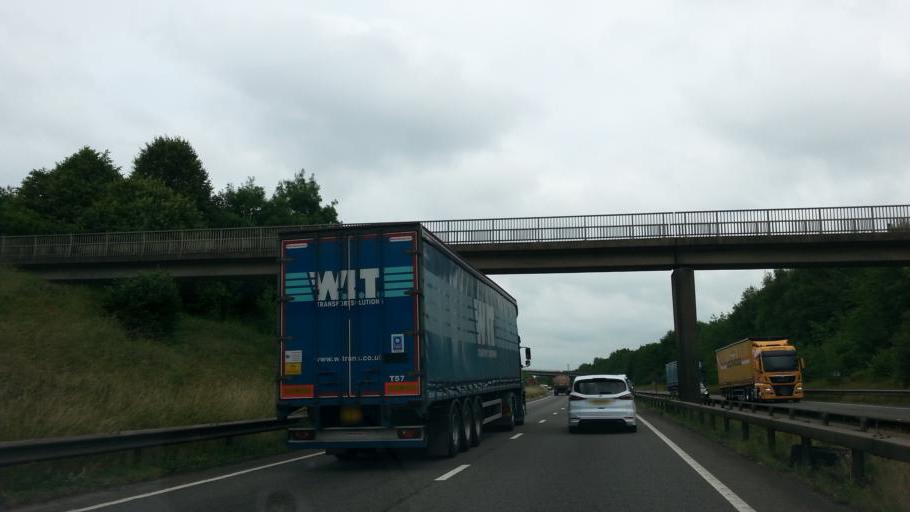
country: GB
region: England
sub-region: Leicestershire
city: Measham
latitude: 52.7095
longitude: -1.5168
